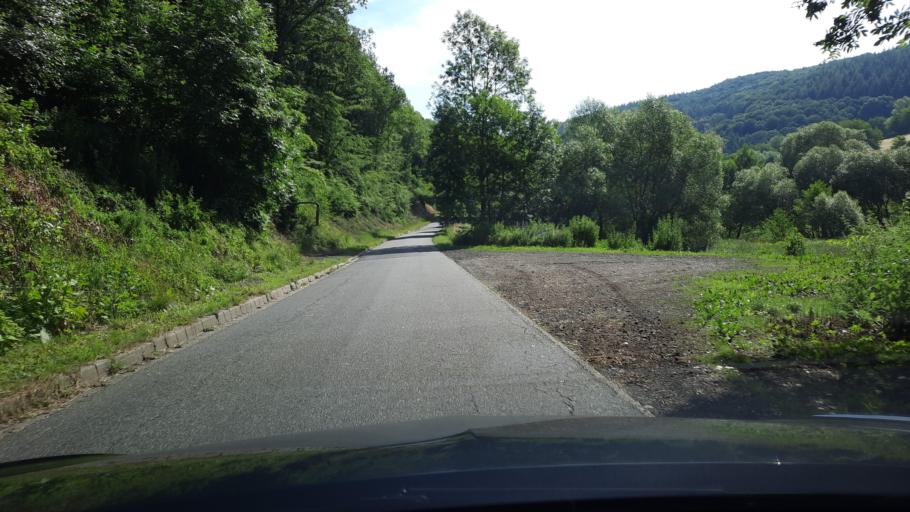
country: DE
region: Rheinland-Pfalz
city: Brenk
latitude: 50.4291
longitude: 7.1655
